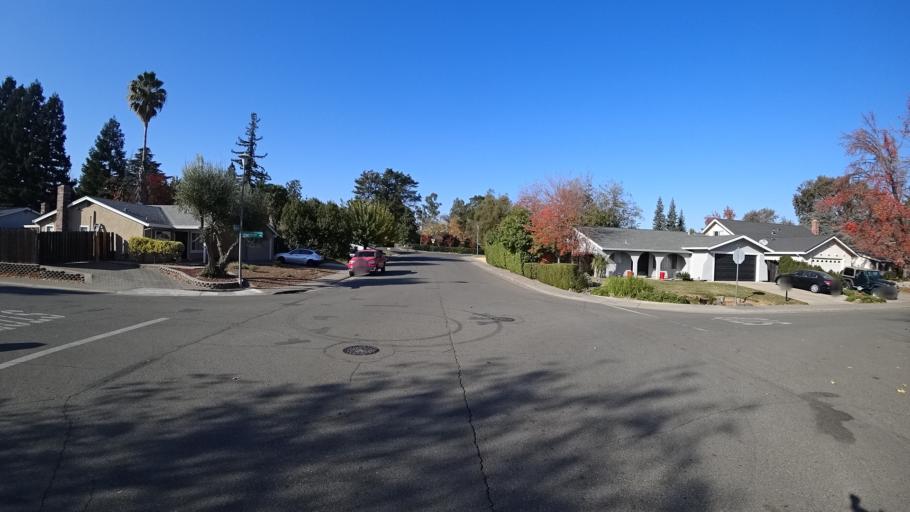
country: US
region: California
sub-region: Sacramento County
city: Citrus Heights
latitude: 38.6950
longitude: -121.2753
